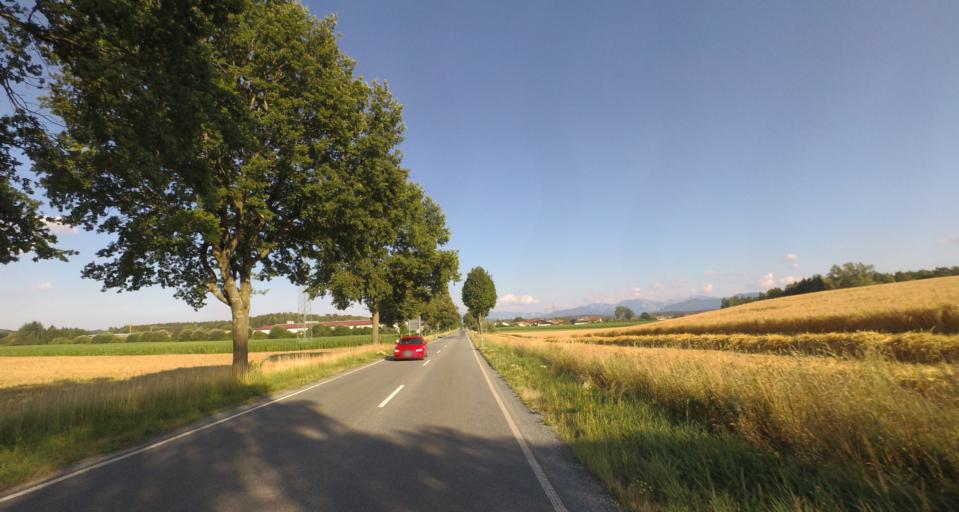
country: DE
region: Bavaria
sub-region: Upper Bavaria
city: Chieming
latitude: 47.9117
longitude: 12.5287
